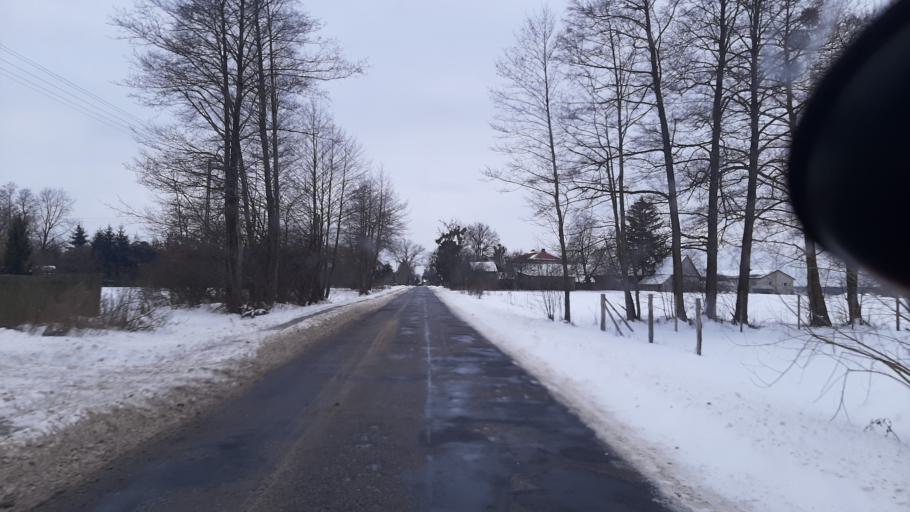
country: PL
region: Lublin Voivodeship
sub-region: Powiat pulawski
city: Markuszow
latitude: 51.4350
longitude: 22.2355
